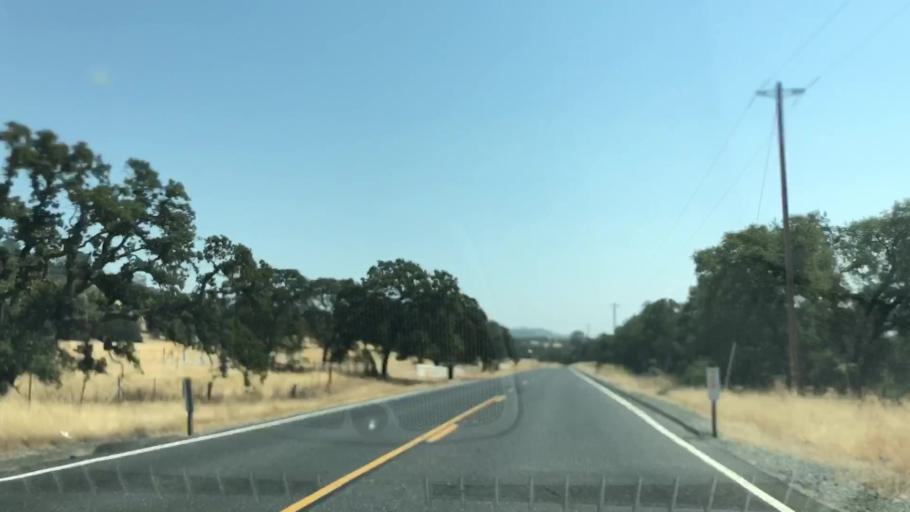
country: US
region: California
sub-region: Calaveras County
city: Copperopolis
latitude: 37.9736
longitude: -120.6315
